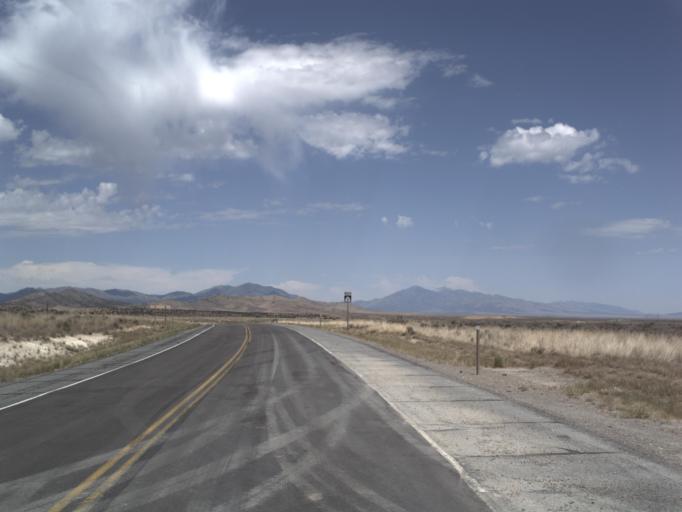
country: US
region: Utah
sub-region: Utah County
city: Eagle Mountain
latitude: 40.0509
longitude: -112.2964
